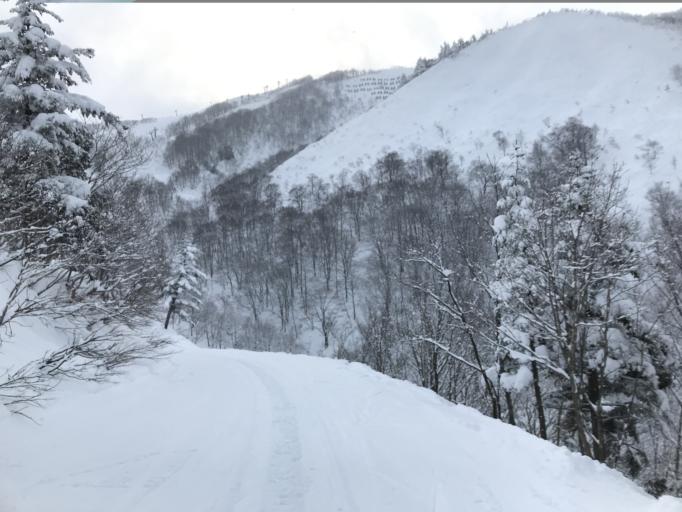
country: JP
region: Nagano
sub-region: Kitaazumi Gun
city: Hakuba
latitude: 36.7013
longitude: 137.8183
